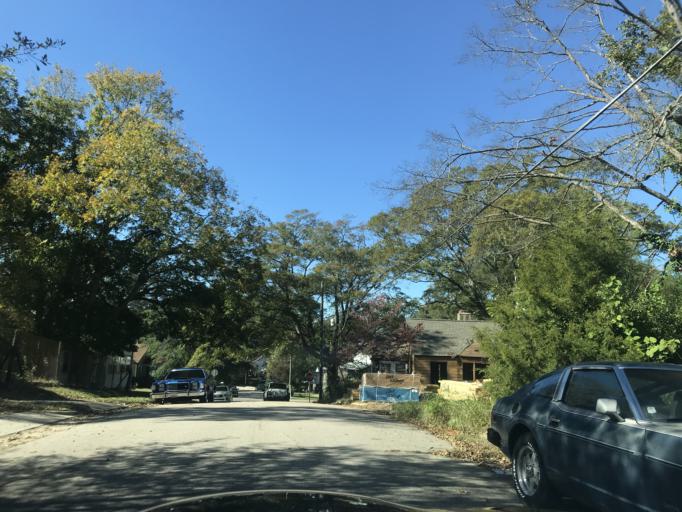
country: US
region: North Carolina
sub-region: Wake County
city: Raleigh
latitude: 35.7941
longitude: -78.6279
